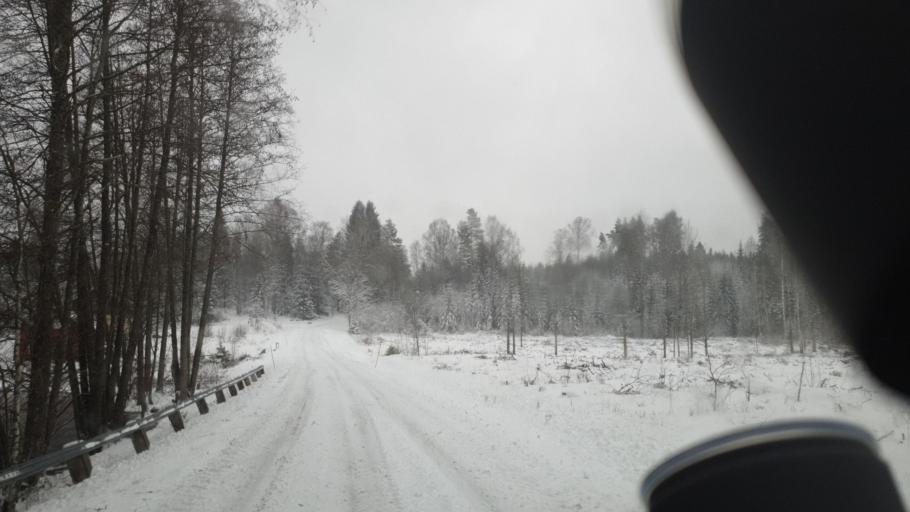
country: SE
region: Vaermland
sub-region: Karlstads Kommun
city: Edsvalla
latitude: 59.6097
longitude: 12.9842
